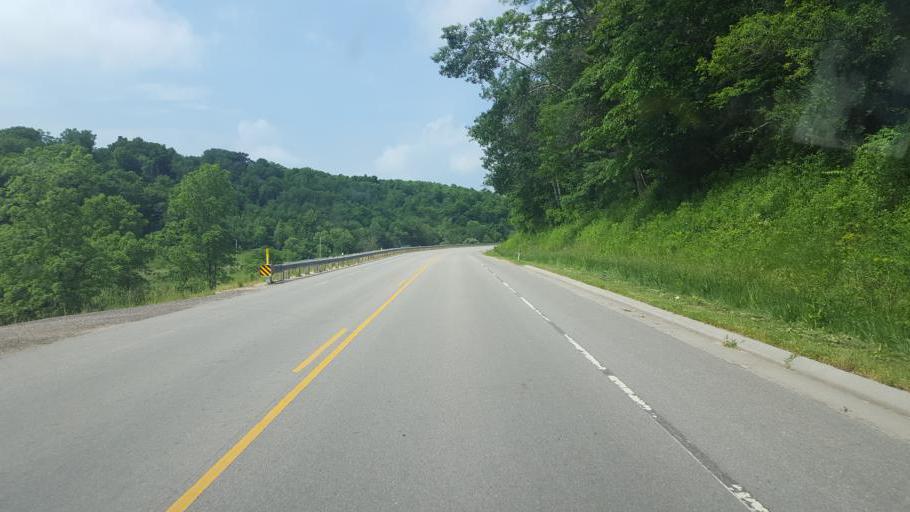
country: US
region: Wisconsin
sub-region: Monroe County
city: Cashton
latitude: 43.7298
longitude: -90.7199
